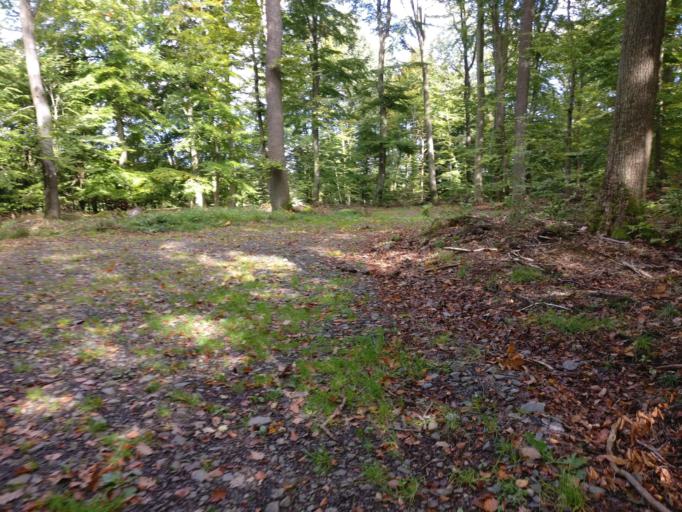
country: DE
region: Hesse
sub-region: Regierungsbezirk Giessen
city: Greifenstein
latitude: 50.6179
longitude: 8.2814
